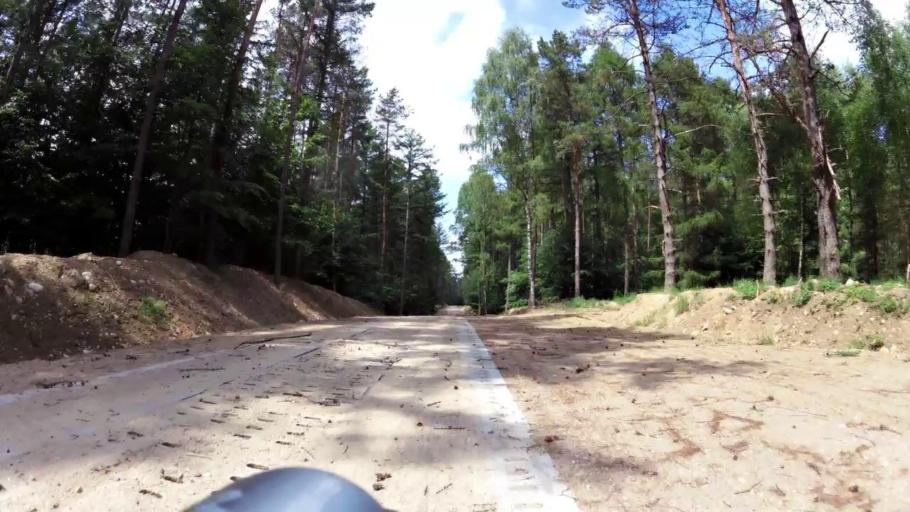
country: PL
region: West Pomeranian Voivodeship
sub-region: Powiat szczecinecki
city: Bialy Bor
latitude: 53.9570
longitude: 16.7564
